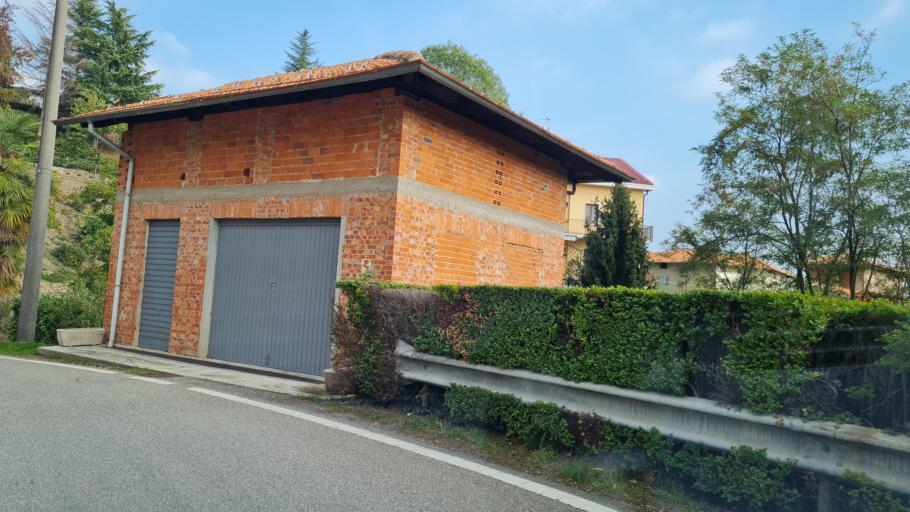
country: IT
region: Piedmont
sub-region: Provincia di Biella
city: Mezzana Mortigliengo
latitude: 45.6267
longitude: 8.1881
